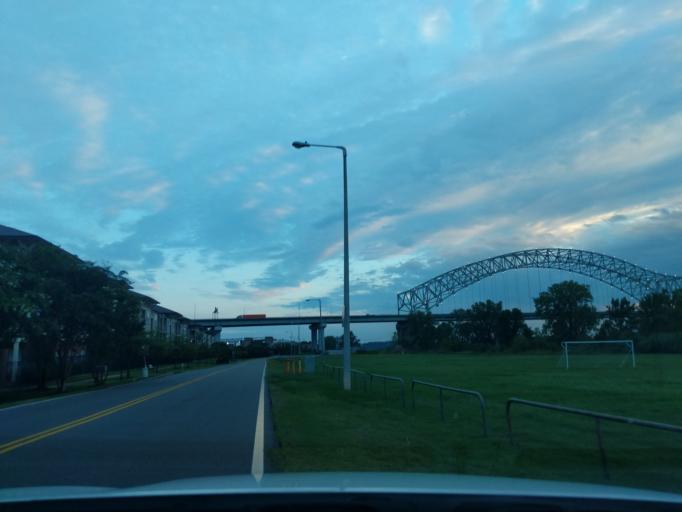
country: US
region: Tennessee
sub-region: Shelby County
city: Memphis
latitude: 35.1566
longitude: -90.0566
